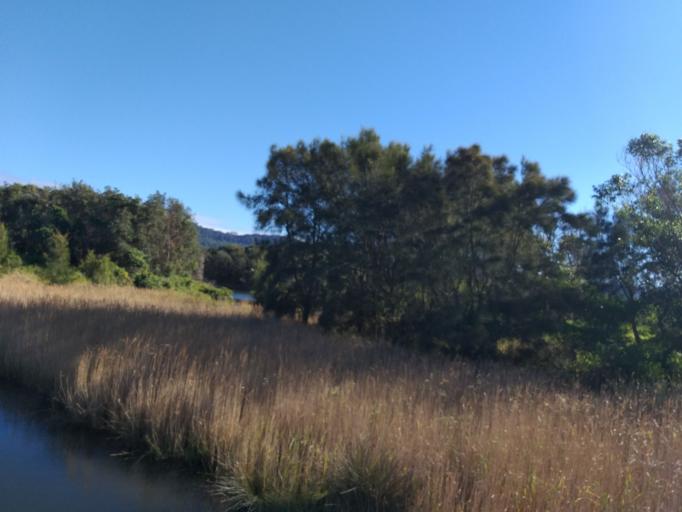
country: AU
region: New South Wales
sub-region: Wollongong
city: East Corrimal
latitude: -34.3640
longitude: 150.9200
